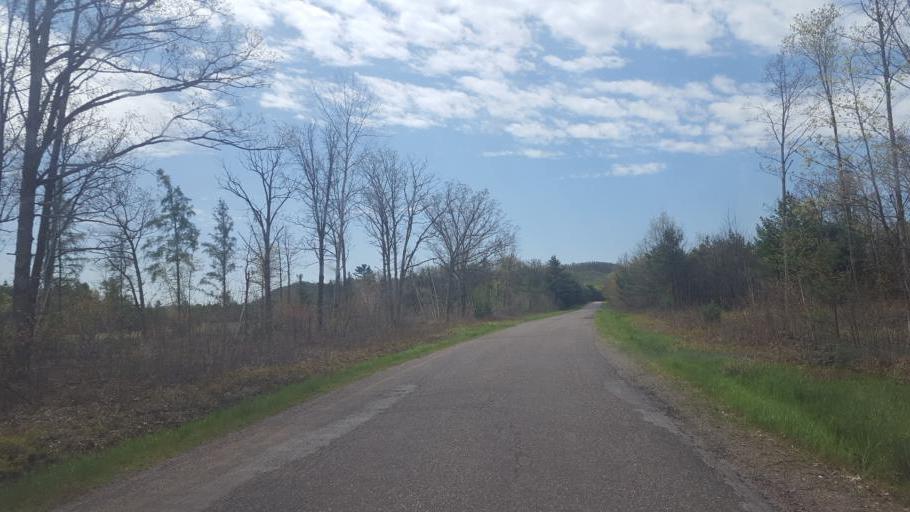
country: US
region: Wisconsin
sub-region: Clark County
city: Neillsville
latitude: 44.3679
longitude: -90.4976
